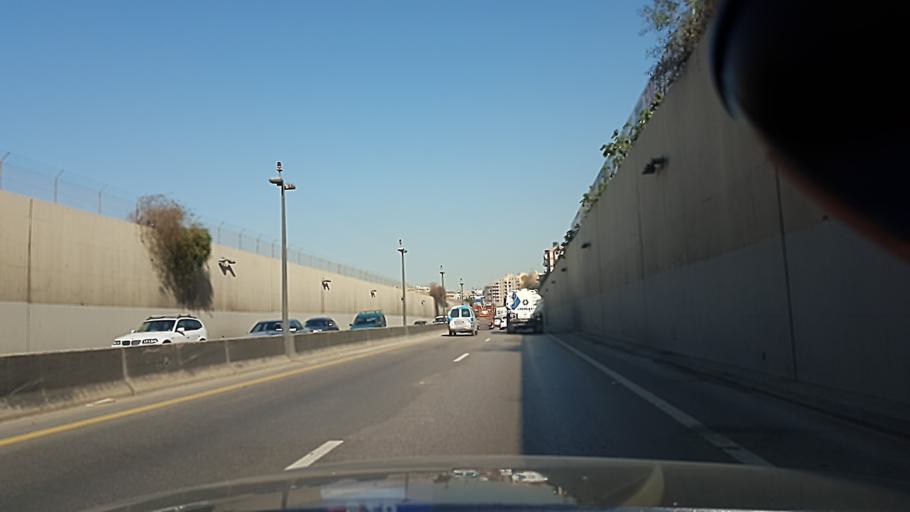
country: LB
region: Mont-Liban
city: Baabda
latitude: 33.8247
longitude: 35.5037
